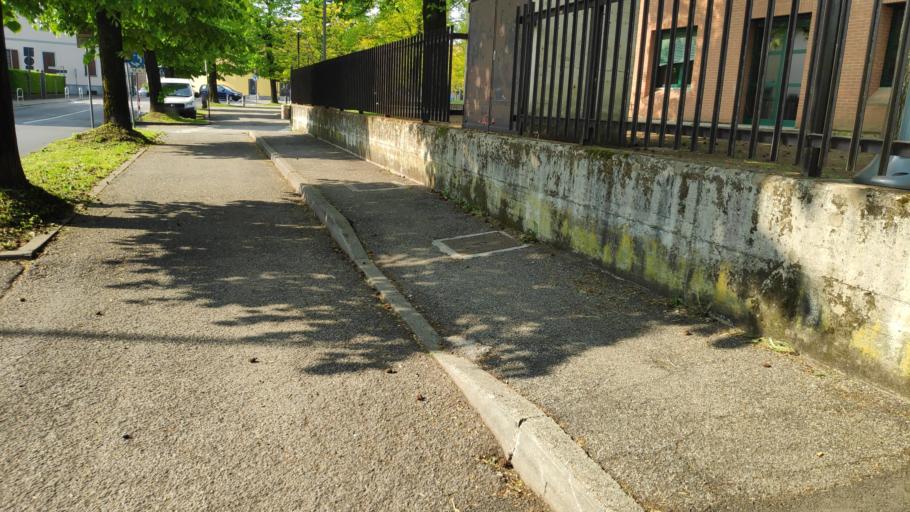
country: IT
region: Lombardy
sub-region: Citta metropolitana di Milano
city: Vizzolo Predabissi
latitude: 45.3567
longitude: 9.3473
